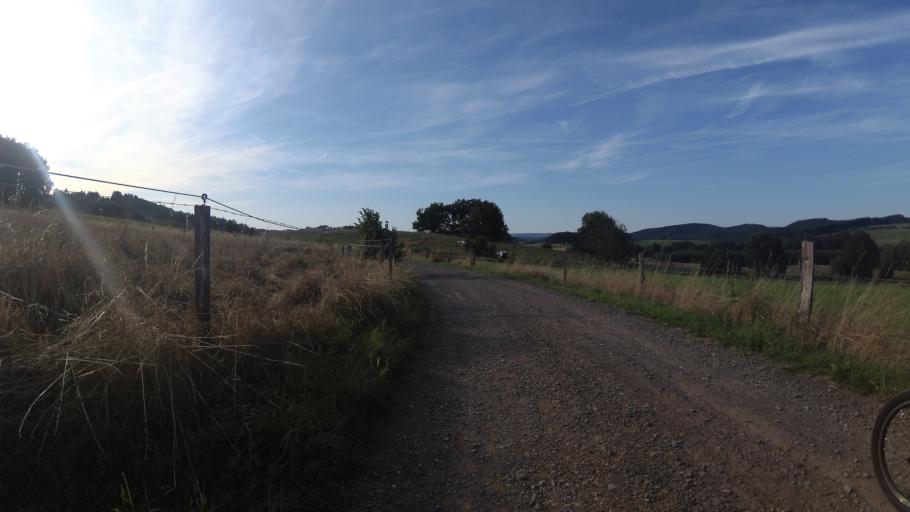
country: DE
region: Saarland
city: Namborn
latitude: 49.5418
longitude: 7.1285
